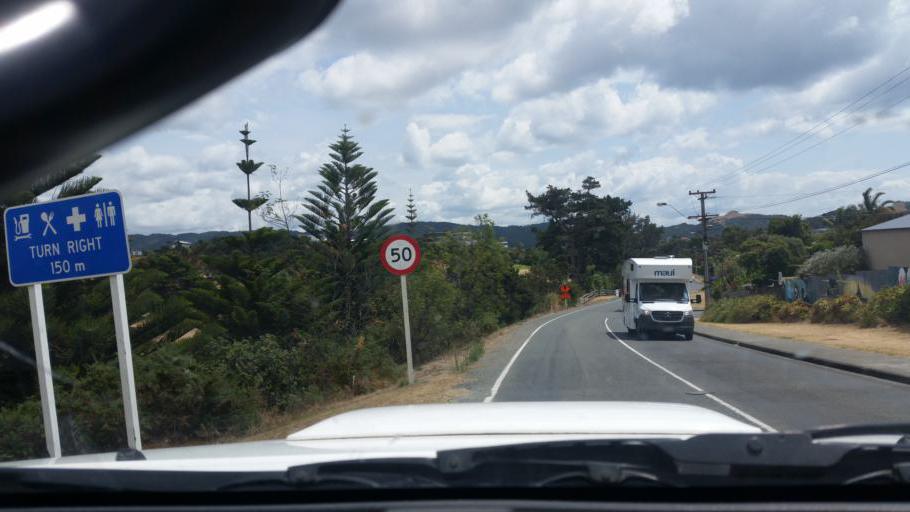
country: NZ
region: Auckland
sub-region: Auckland
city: Wellsford
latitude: -36.0972
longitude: 174.5866
